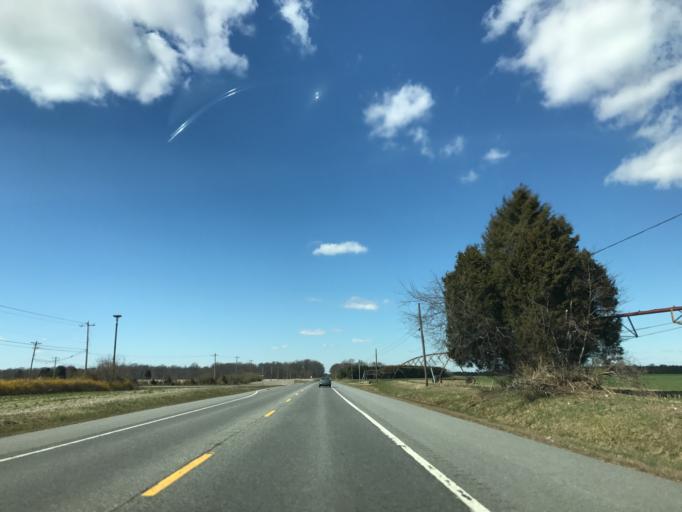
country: US
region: Maryland
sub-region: Queen Anne's County
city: Kingstown
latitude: 39.1727
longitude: -75.9916
